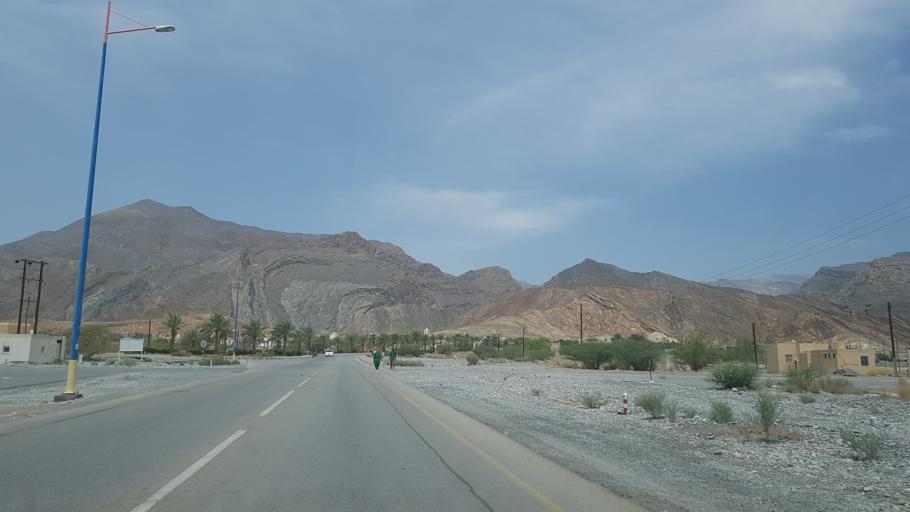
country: OM
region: Muhafazat ad Dakhiliyah
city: Izki
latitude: 22.9144
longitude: 57.6733
